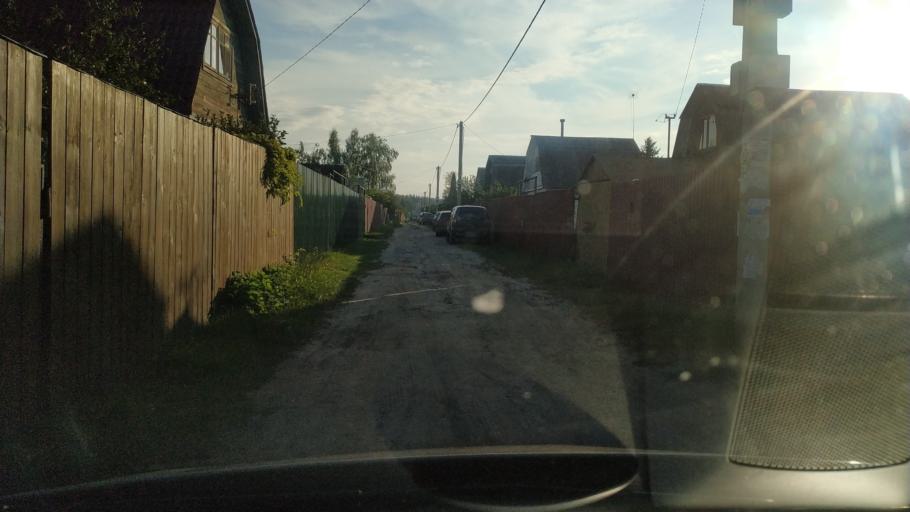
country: RU
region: Moskovskaya
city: Roshal'
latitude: 55.6449
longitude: 39.7953
